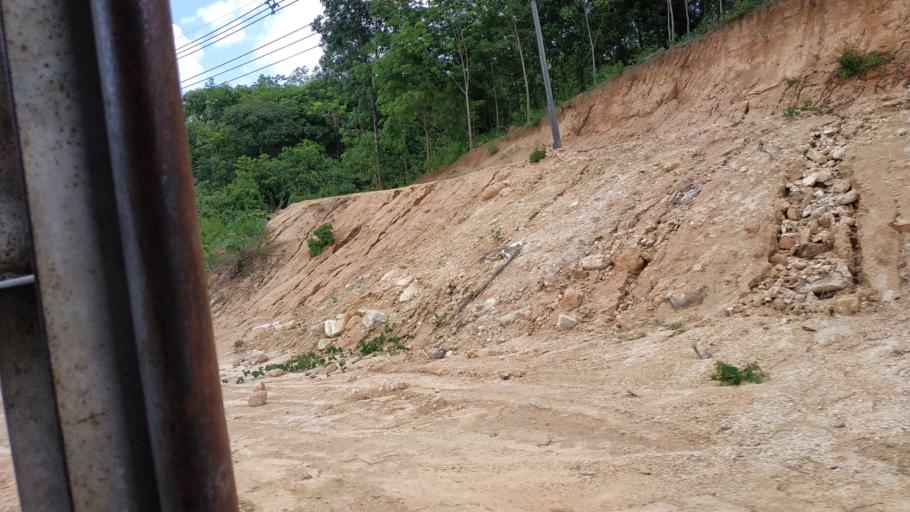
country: MM
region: Mon
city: Kyaikto
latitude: 17.4183
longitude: 97.0710
